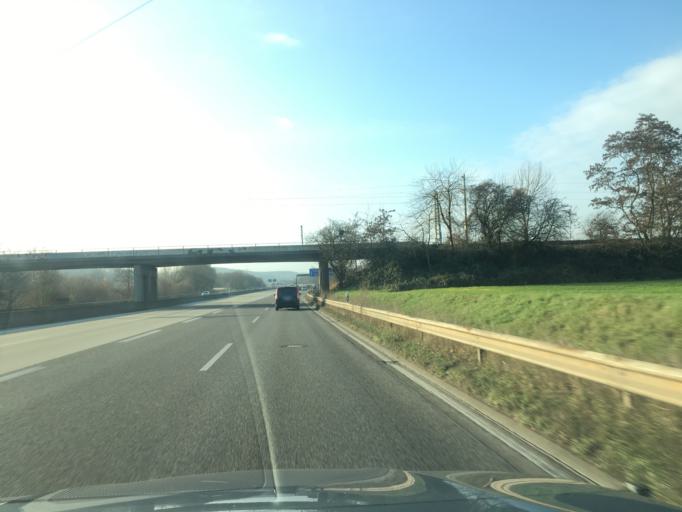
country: DE
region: Rheinland-Pfalz
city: Kaltenengers
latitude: 50.3964
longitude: 7.5528
